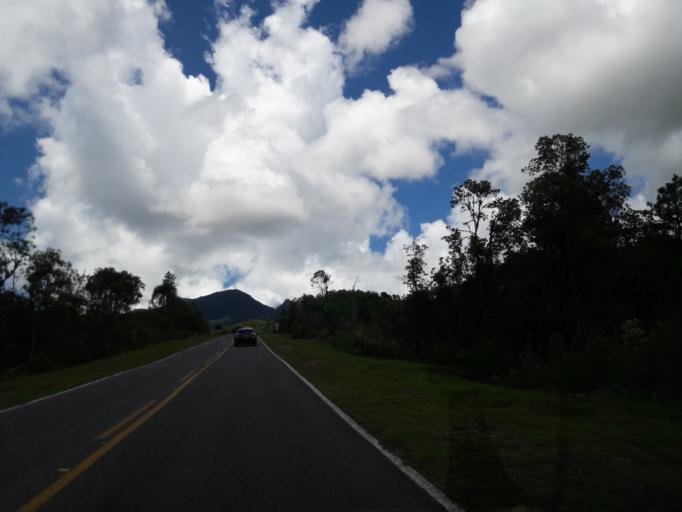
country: BR
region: Parana
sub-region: Campina Grande Do Sul
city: Campina Grande do Sul
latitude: -25.3193
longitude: -48.9274
